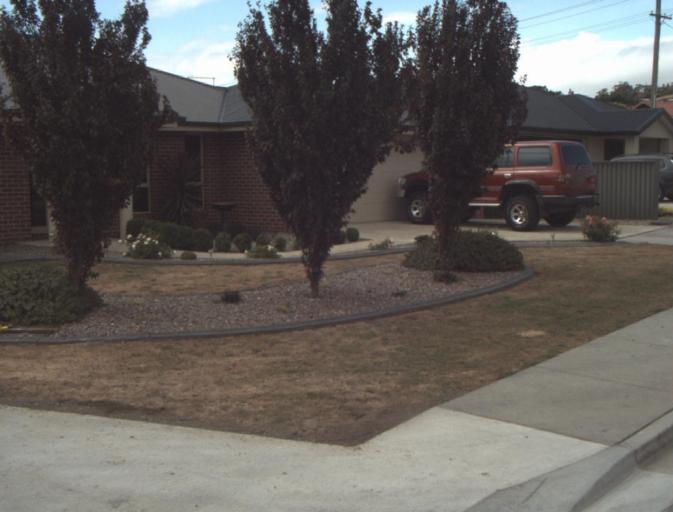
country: AU
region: Tasmania
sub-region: Launceston
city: Newstead
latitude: -41.4606
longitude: 147.2013
